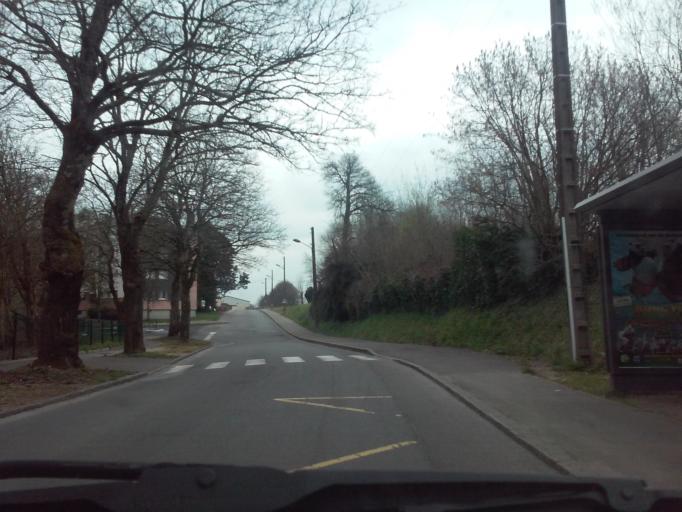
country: FR
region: Brittany
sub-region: Departement d'Ille-et-Vilaine
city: Fougeres
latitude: 48.3450
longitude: -1.1887
